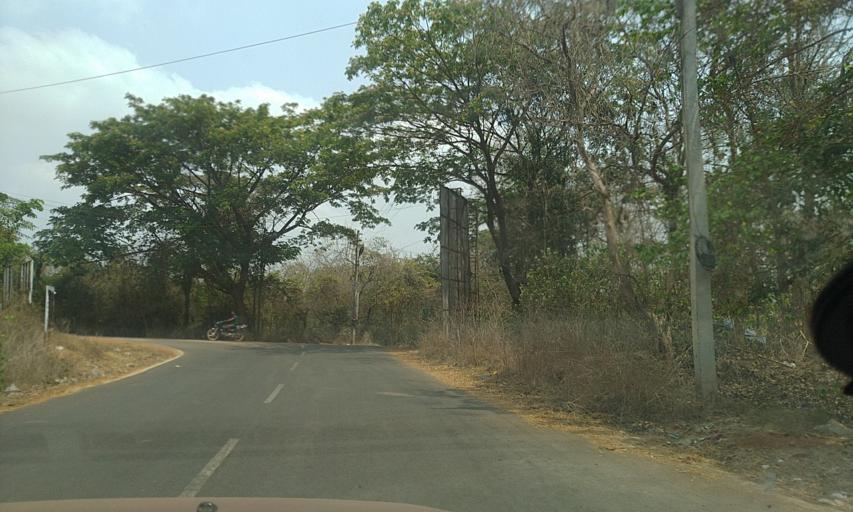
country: IN
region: Goa
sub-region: North Goa
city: Jua
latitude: 15.4936
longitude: 73.9109
